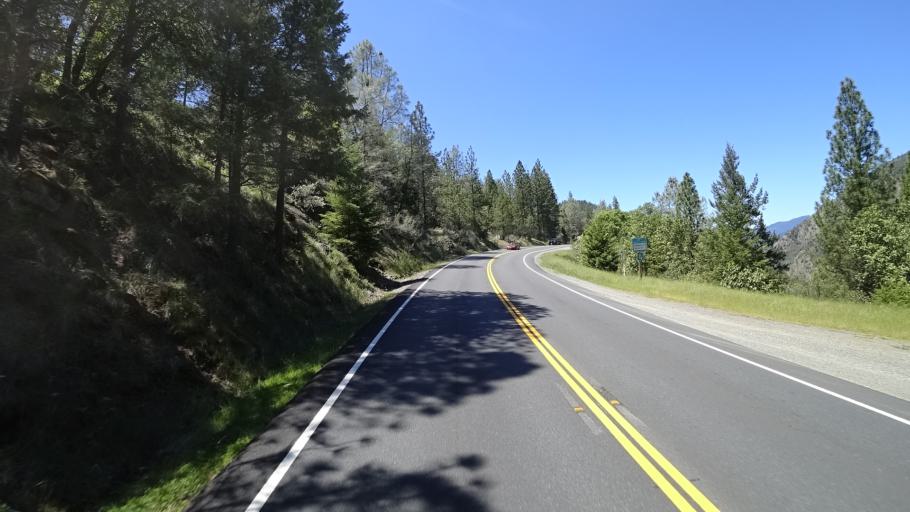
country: US
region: California
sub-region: Humboldt County
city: Willow Creek
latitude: 40.8056
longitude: -123.4701
